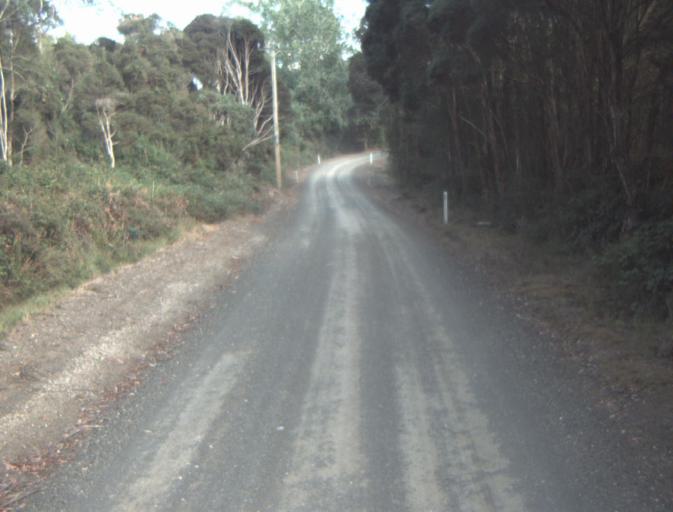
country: AU
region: Tasmania
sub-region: Launceston
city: Mayfield
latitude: -41.2743
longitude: 147.1845
